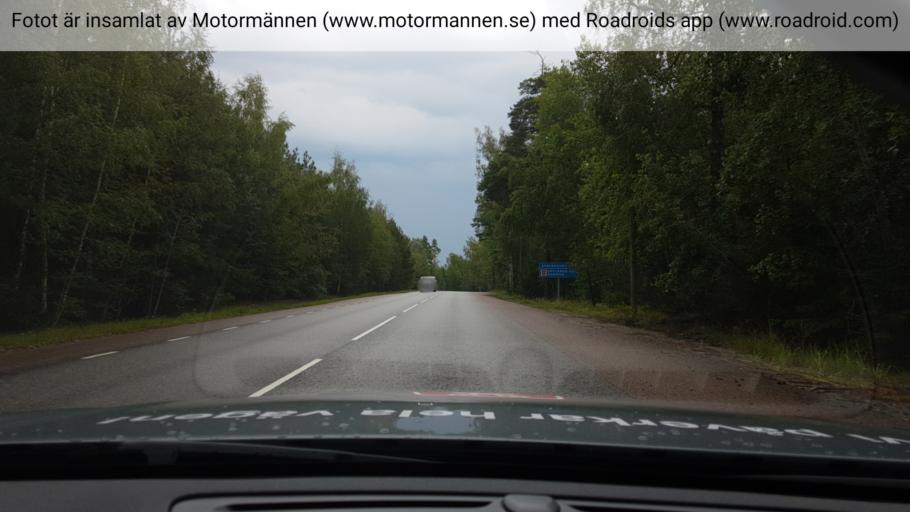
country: SE
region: Uppsala
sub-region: Habo Kommun
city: Balsta
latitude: 59.5421
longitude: 17.5617
